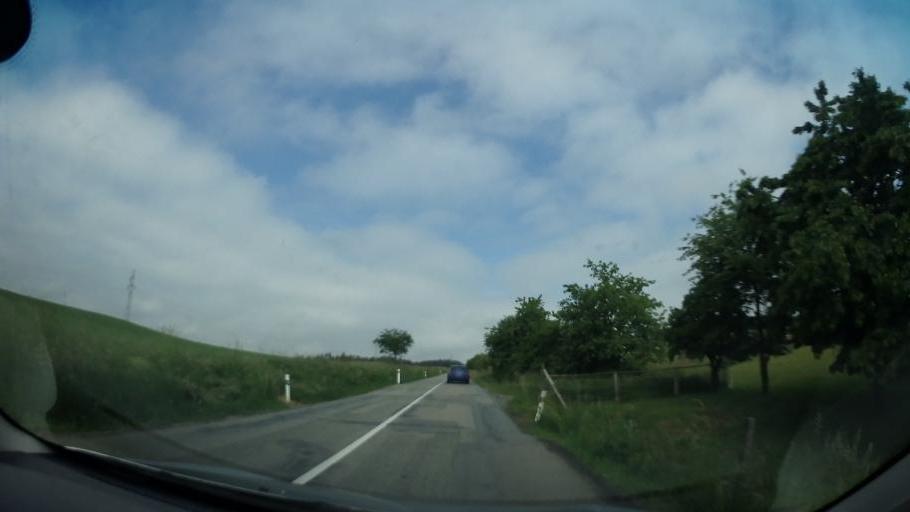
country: CZ
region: South Moravian
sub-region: Okres Brno-Venkov
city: Dolni Loucky
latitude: 49.3794
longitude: 16.3464
